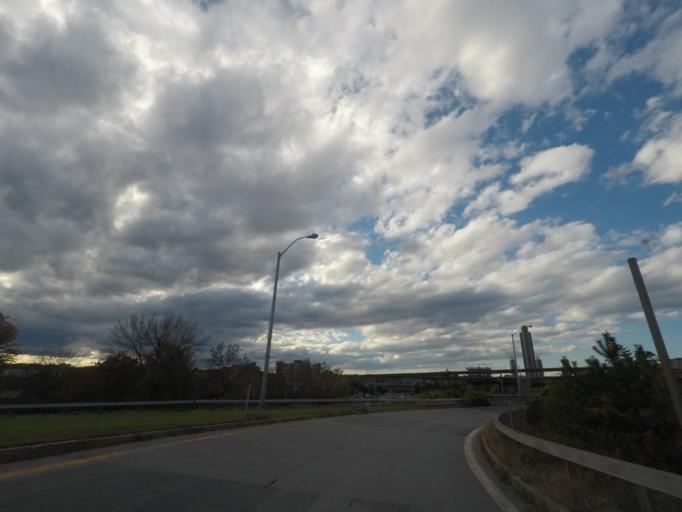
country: US
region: New York
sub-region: Rensselaer County
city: Rensselaer
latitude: 42.6410
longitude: -73.7470
